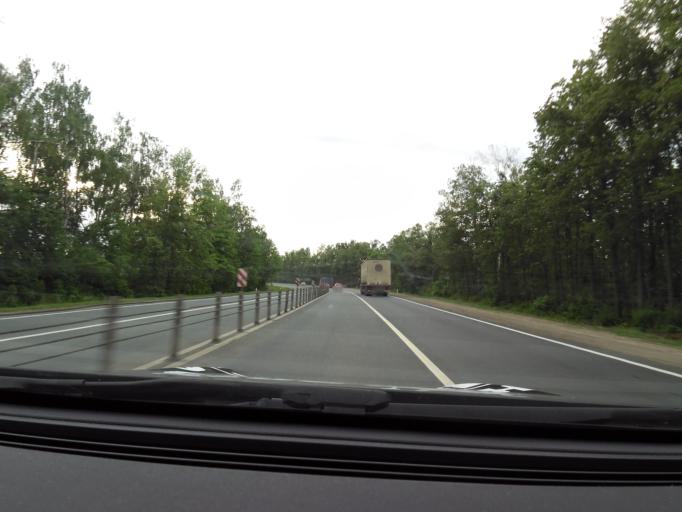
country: RU
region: Chuvashia
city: Tsivil'sk
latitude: 55.9125
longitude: 47.4207
